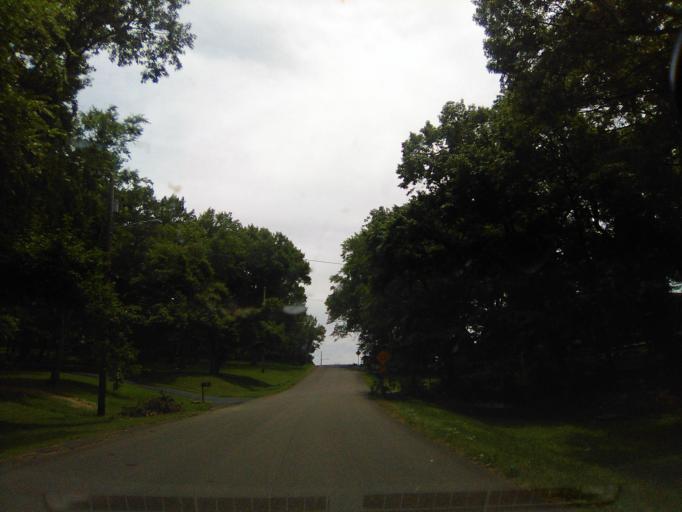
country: US
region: Tennessee
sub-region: Davidson County
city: Belle Meade
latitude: 36.1194
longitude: -86.8959
